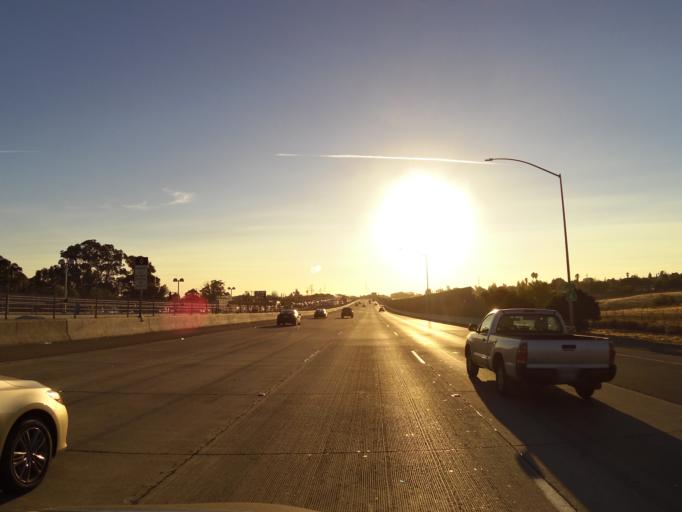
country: US
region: California
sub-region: Contra Costa County
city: Bay Point
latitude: 38.0187
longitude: -121.9372
